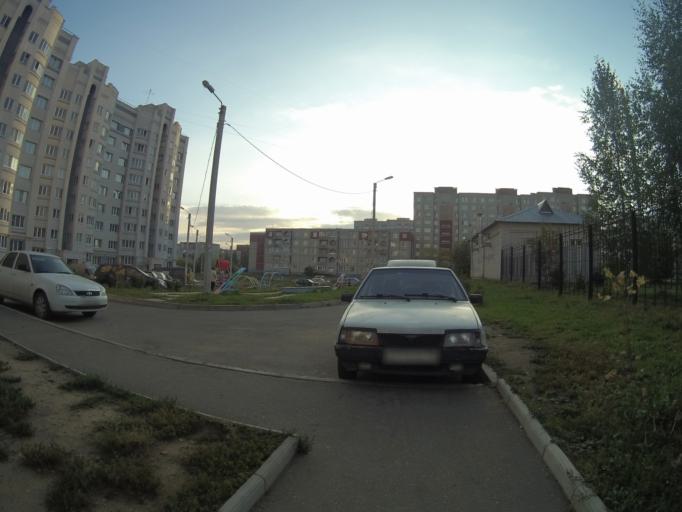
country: RU
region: Vladimir
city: Vladimir
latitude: 56.1042
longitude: 40.3560
